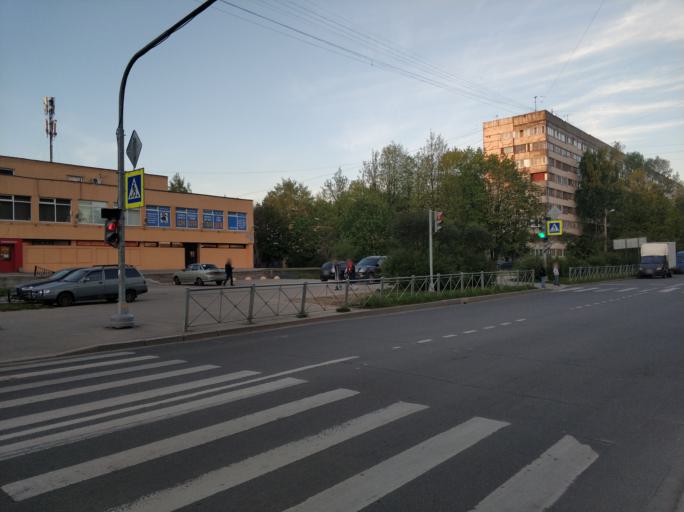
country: RU
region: St.-Petersburg
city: Grazhdanka
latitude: 60.0457
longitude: 30.3951
